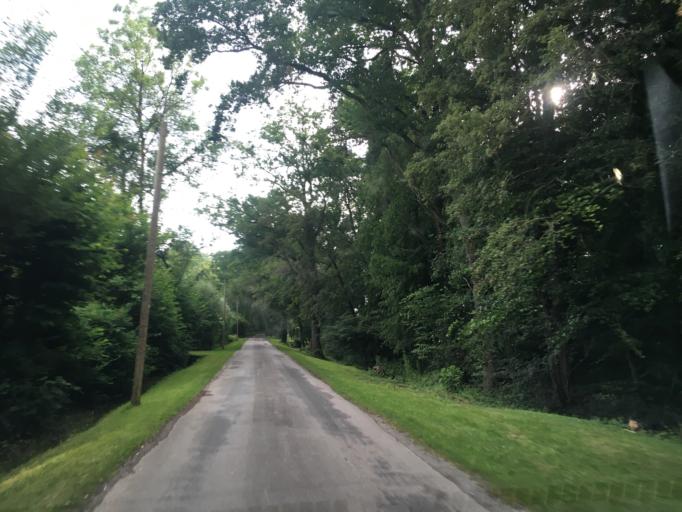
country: DE
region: North Rhine-Westphalia
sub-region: Regierungsbezirk Munster
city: Altenberge
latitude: 52.0228
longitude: 7.5221
